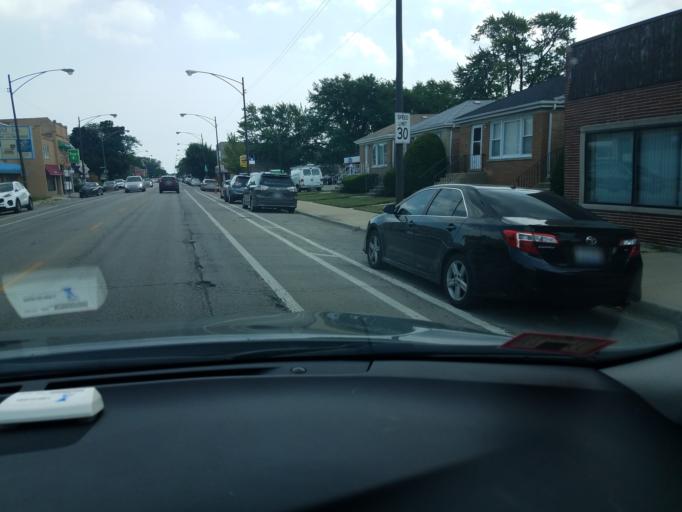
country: US
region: Illinois
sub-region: Cook County
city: Harwood Heights
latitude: 41.9897
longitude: -87.7774
